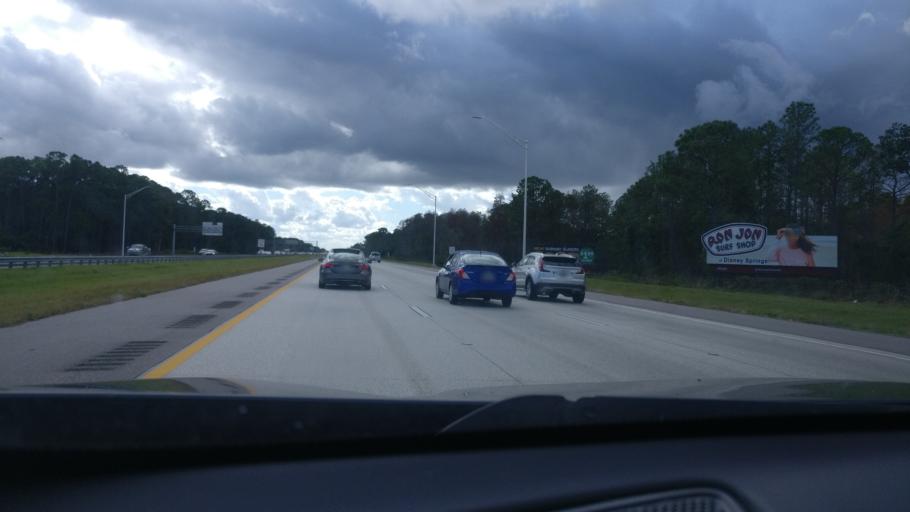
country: US
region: Florida
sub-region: Volusia County
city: Samsula-Spruce Creek
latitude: 29.1263
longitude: -81.1292
